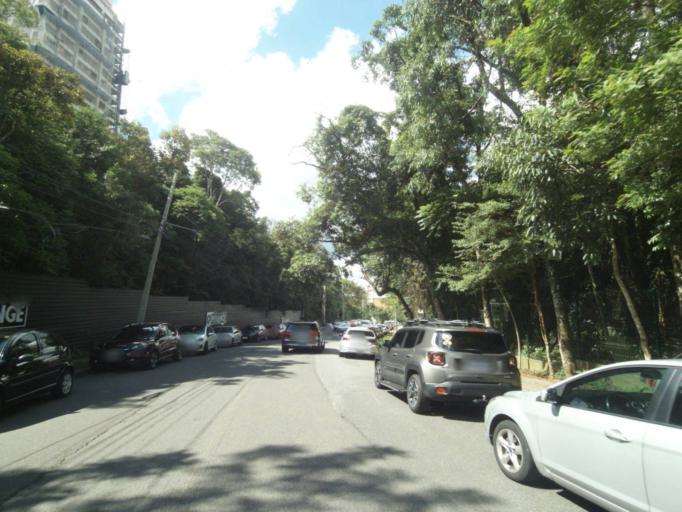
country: BR
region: Parana
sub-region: Curitiba
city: Curitiba
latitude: -25.4392
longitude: -49.3358
